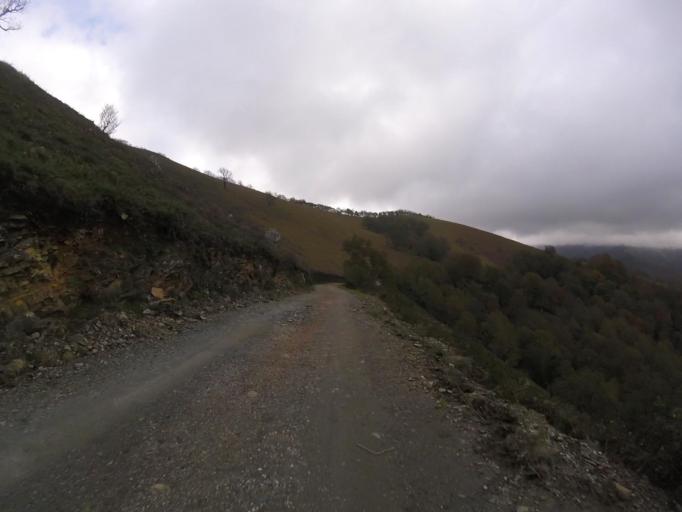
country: ES
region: Navarre
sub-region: Provincia de Navarra
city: Goizueta
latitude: 43.1940
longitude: -1.8184
